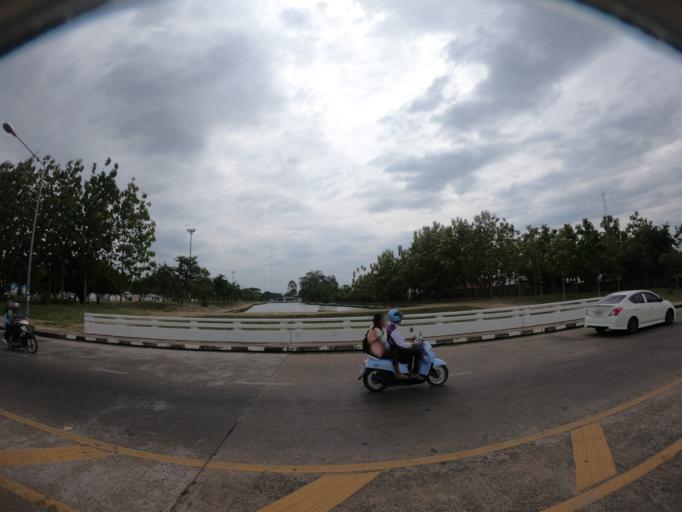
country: TH
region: Roi Et
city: Roi Et
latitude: 16.0541
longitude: 103.6433
